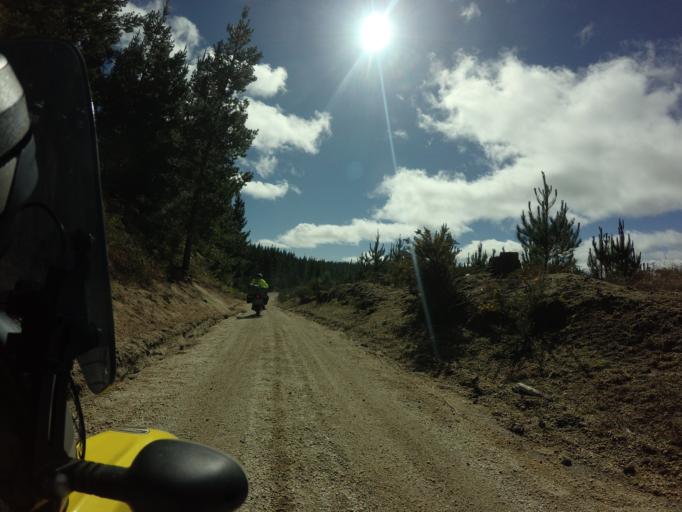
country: NZ
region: Bay of Plenty
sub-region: Whakatane District
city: Murupara
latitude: -38.8227
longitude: 176.5500
